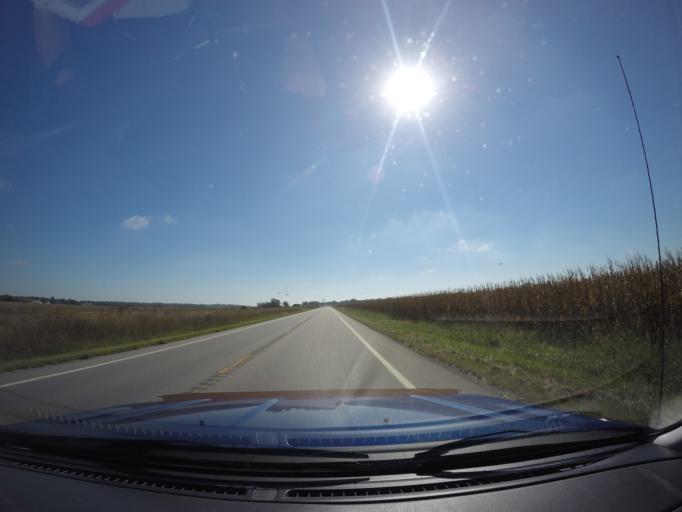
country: US
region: Kansas
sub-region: Shawnee County
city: Silver Lake
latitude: 39.1100
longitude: -95.8786
